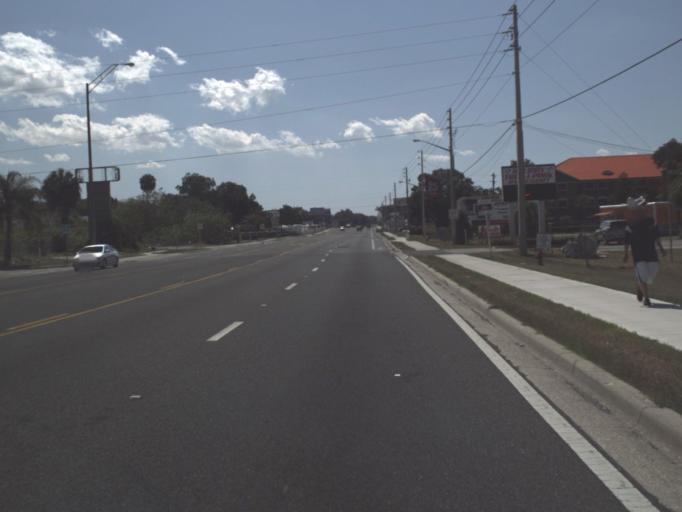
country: US
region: Florida
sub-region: Marion County
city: Ocala
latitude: 29.1864
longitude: -82.1876
